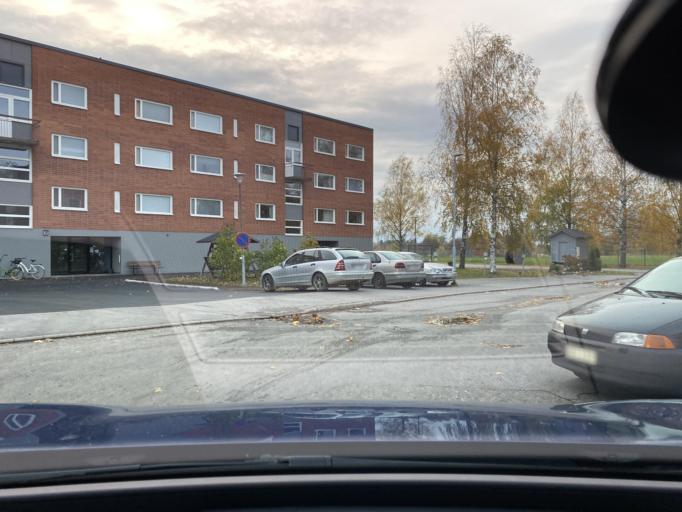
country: FI
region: Satakunta
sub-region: Pori
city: Huittinen
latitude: 61.1780
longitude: 22.6931
